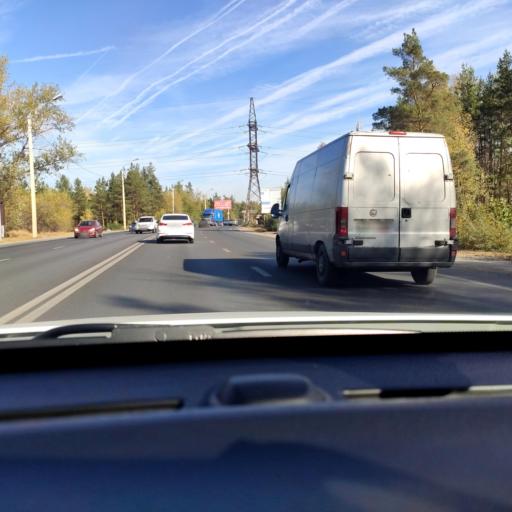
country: RU
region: Voronezj
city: Pridonskoy
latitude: 51.6790
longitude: 39.1150
